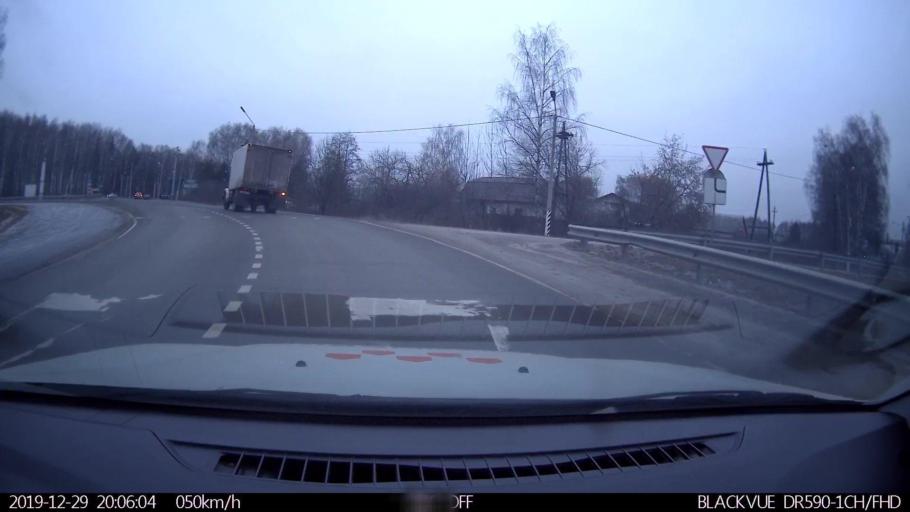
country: RU
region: Nizjnij Novgorod
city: Neklyudovo
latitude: 56.3948
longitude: 44.0082
